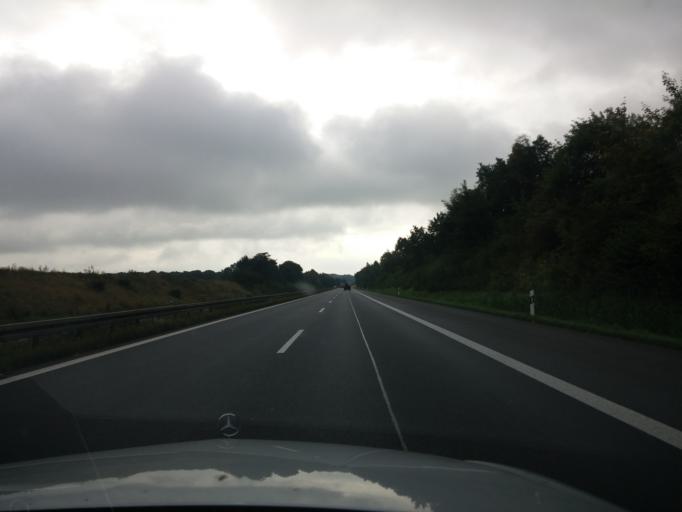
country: DE
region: Brandenburg
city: Gerdshagen
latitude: 53.2063
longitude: 12.2596
